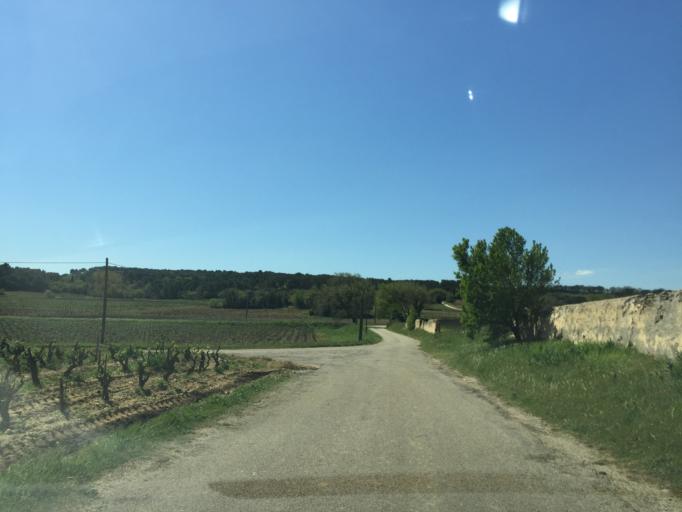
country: FR
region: Provence-Alpes-Cote d'Azur
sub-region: Departement du Vaucluse
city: Courthezon
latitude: 44.0827
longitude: 4.8544
